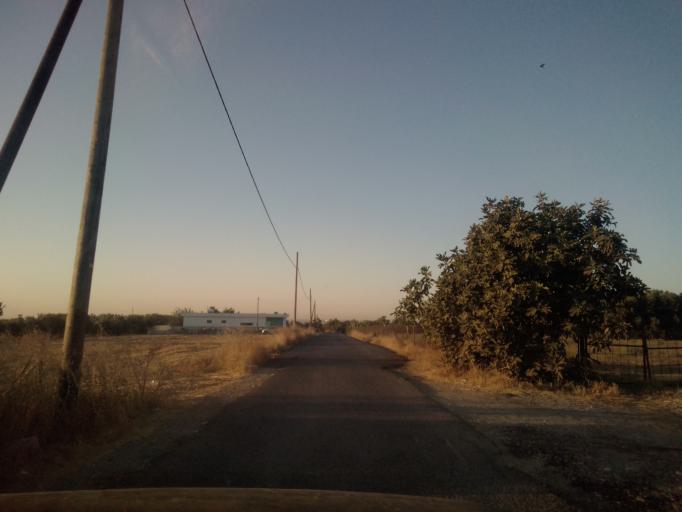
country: CY
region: Limassol
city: Ypsonas
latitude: 34.6764
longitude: 32.9669
